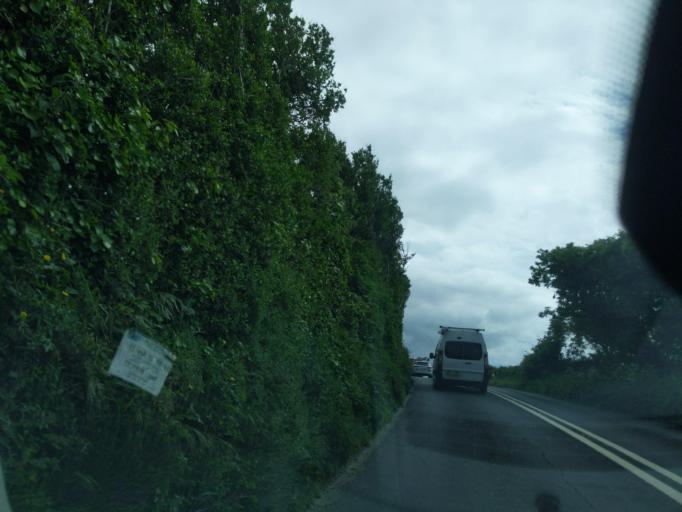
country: GB
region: England
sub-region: Cornwall
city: Perranporth
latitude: 50.3212
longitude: -5.1360
